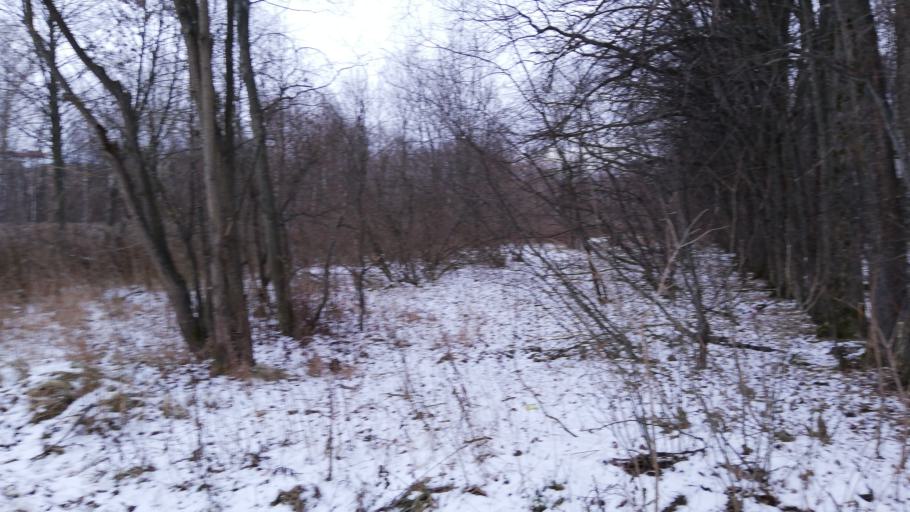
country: RU
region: Jaroslavl
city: Yaroslavl
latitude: 57.7246
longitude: 39.8172
